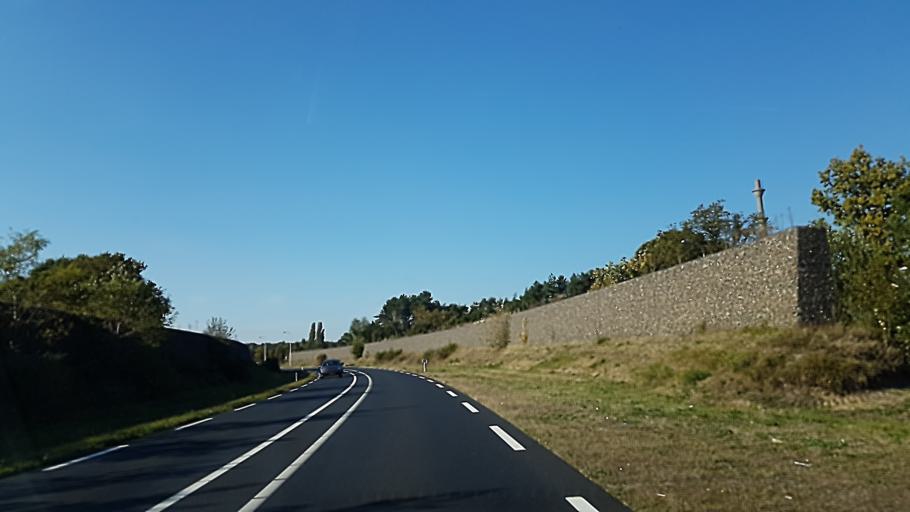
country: NL
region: North Brabant
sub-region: Gemeente Woensdrecht
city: Woensdrecht
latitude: 51.4364
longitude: 4.3372
